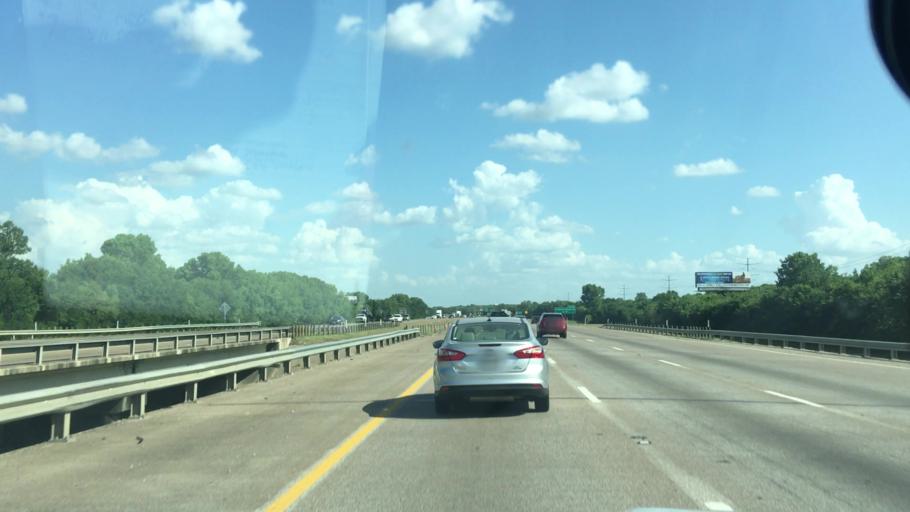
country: US
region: Texas
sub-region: Dallas County
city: Hutchins
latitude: 32.6949
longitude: -96.7509
